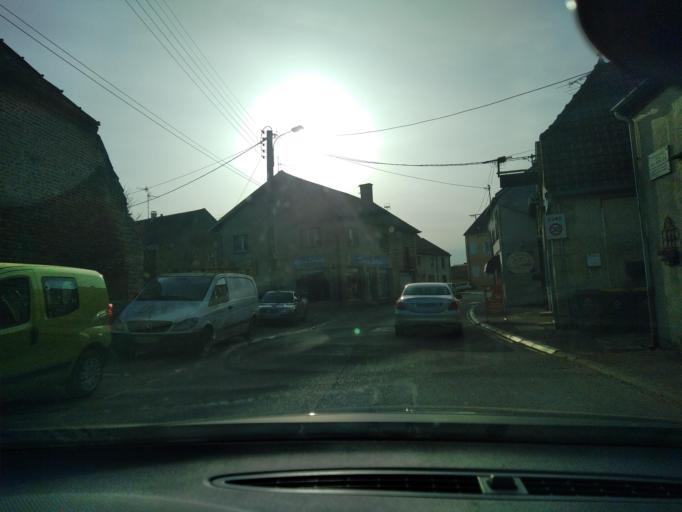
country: FR
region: Franche-Comte
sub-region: Departement du Jura
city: Chaussin
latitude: 46.9675
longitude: 5.4102
